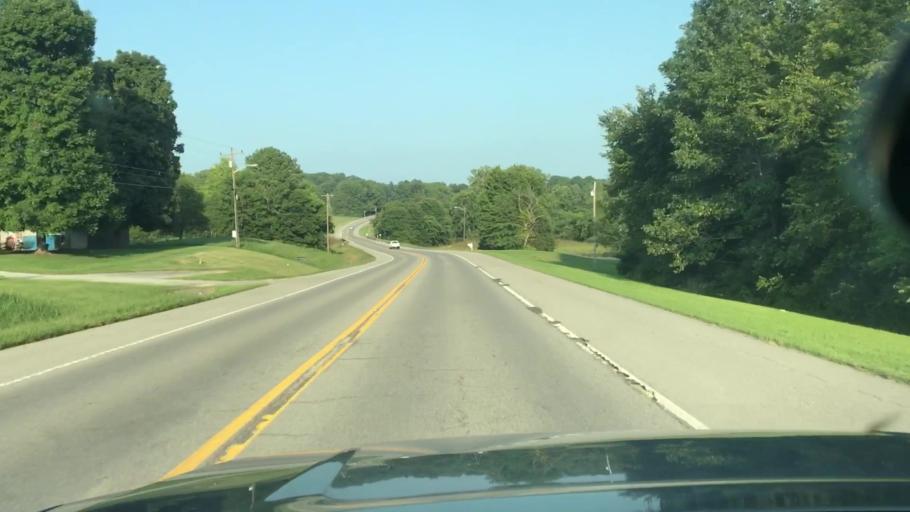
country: US
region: Tennessee
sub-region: Sumner County
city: Portland
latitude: 36.5786
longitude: -86.4616
